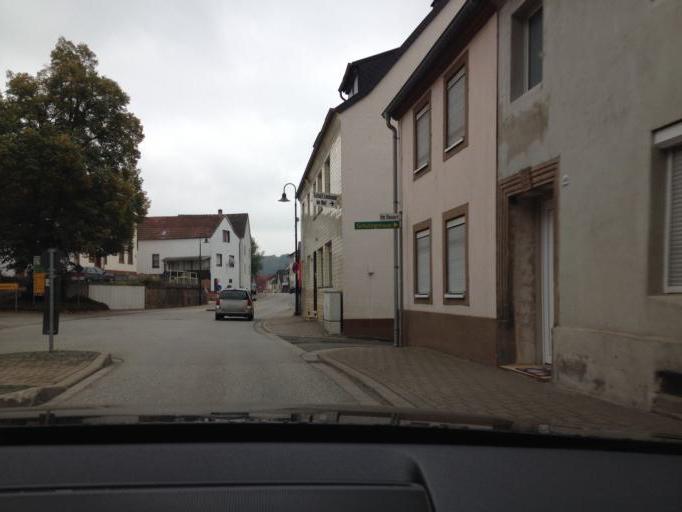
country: DE
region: Rheinland-Pfalz
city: Contwig
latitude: 49.2499
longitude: 7.4253
